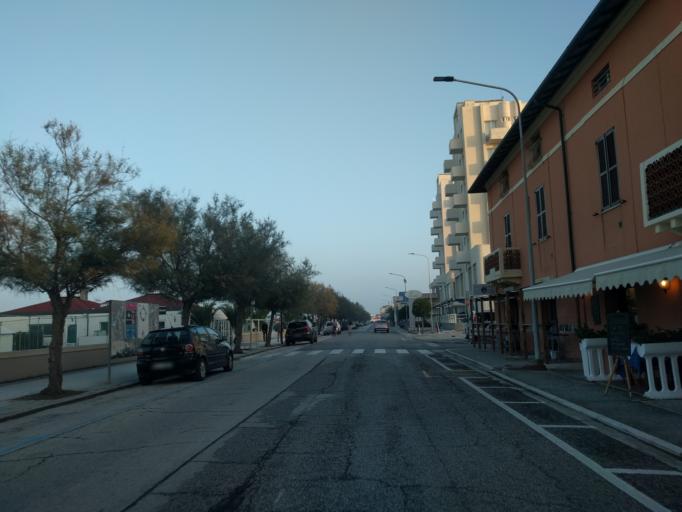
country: IT
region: The Marches
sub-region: Provincia di Ancona
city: Senigallia
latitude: 43.7229
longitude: 13.2138
